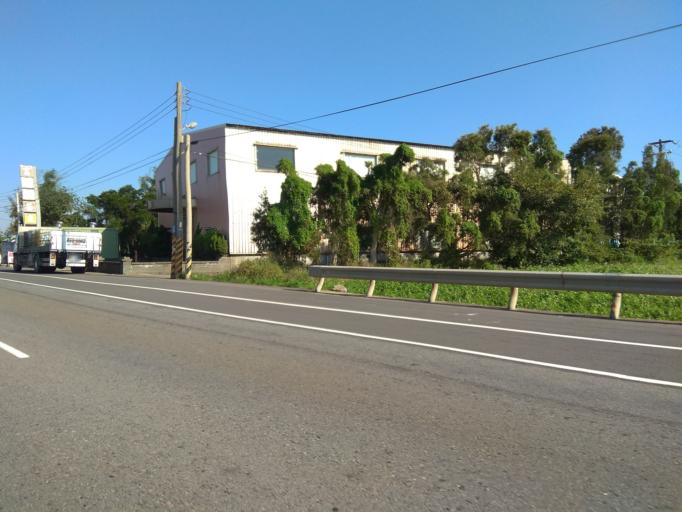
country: TW
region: Taiwan
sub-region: Hsinchu
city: Zhubei
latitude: 25.0266
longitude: 121.0887
